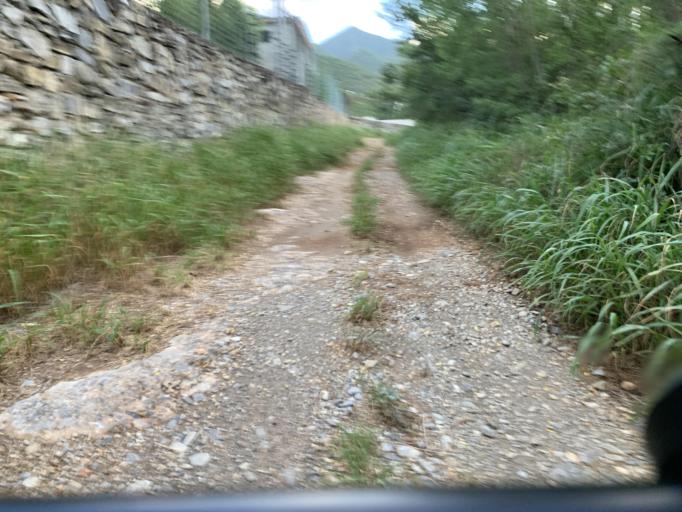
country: MX
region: Nuevo Leon
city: Santiago
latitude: 25.5079
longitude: -100.1827
